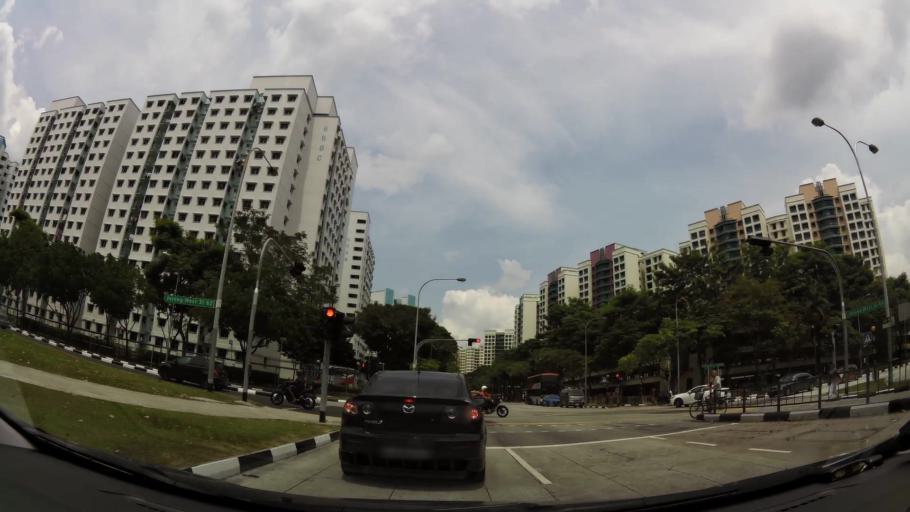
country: MY
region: Johor
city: Johor Bahru
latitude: 1.3408
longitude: 103.7038
